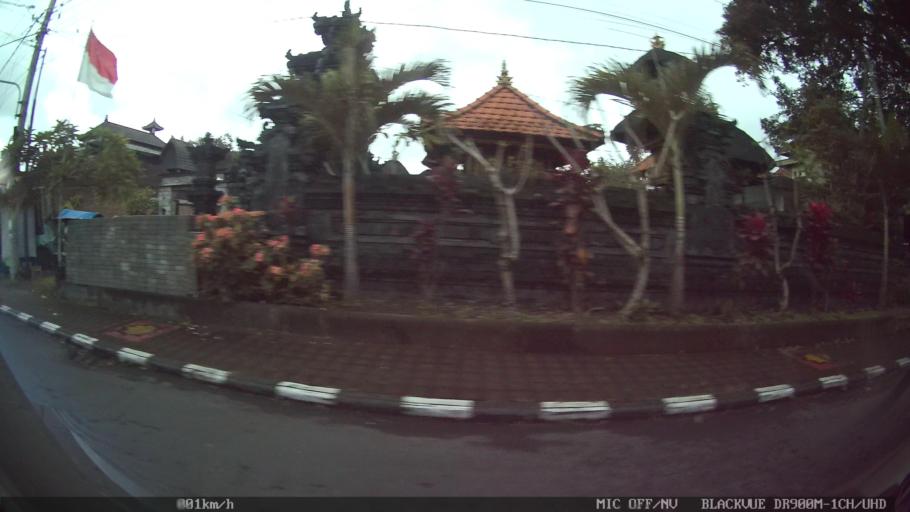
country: ID
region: Bali
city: Banjar Sempidi
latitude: -8.5241
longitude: 115.2028
